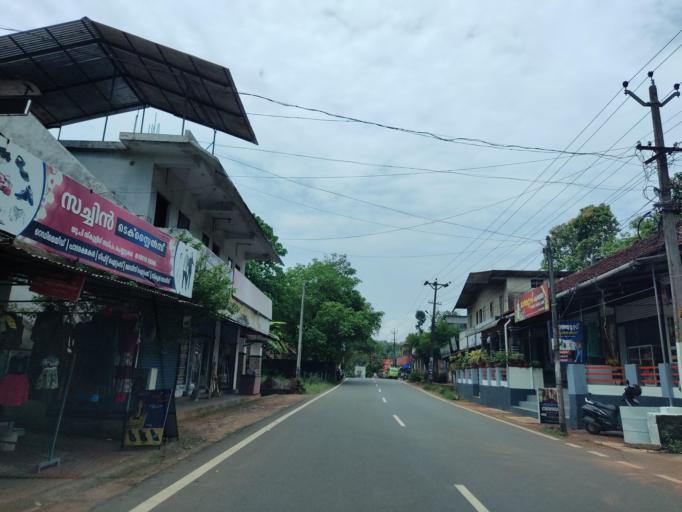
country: IN
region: Kerala
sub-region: Alappuzha
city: Chengannur
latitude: 9.2868
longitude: 76.6154
